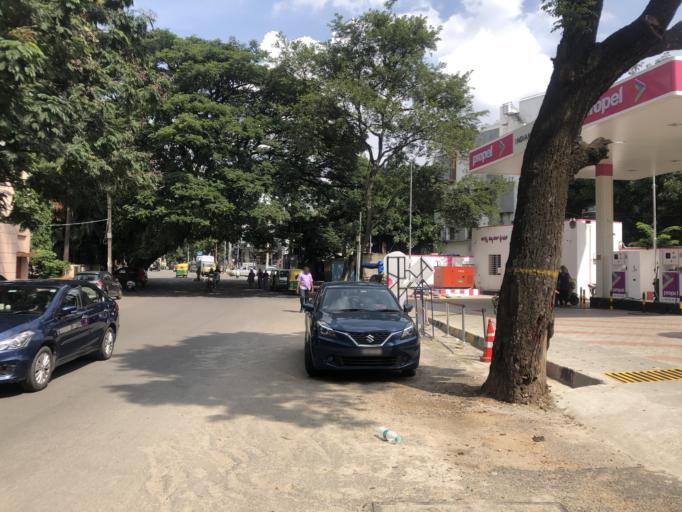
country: IN
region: Karnataka
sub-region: Bangalore Urban
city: Bangalore
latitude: 12.9385
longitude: 77.5492
